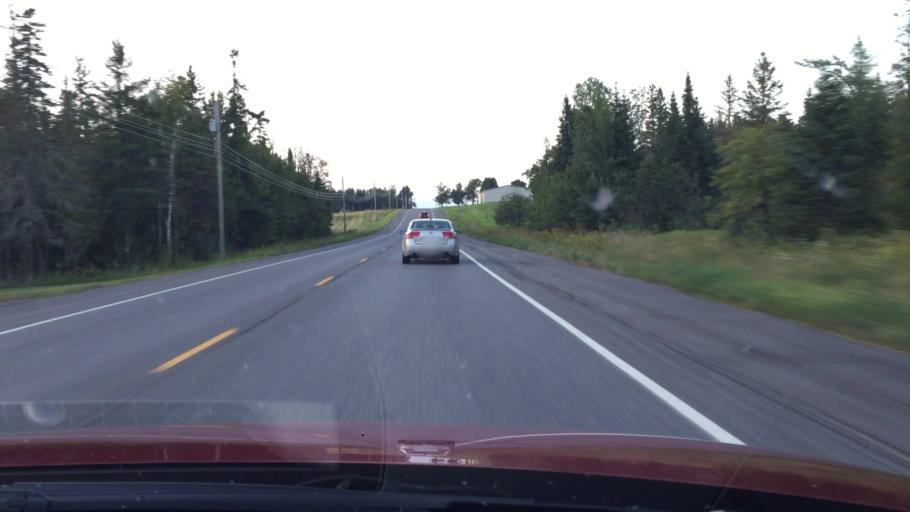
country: CA
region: New Brunswick
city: Florenceville-Bristol
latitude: 46.4040
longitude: -67.8431
